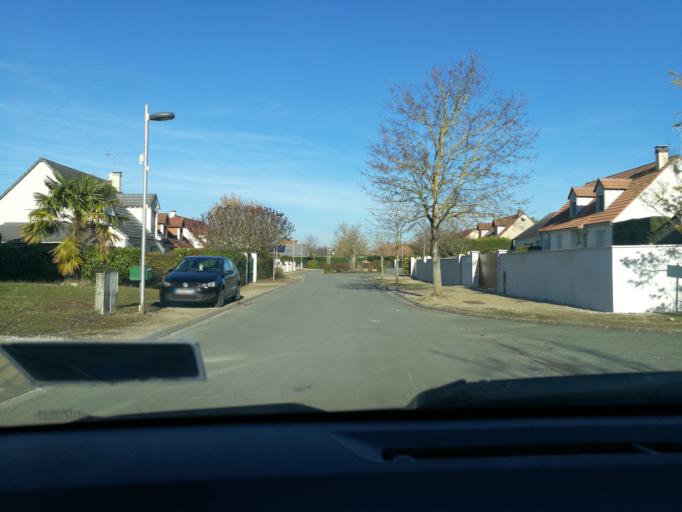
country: FR
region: Centre
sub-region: Departement du Loiret
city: Chaingy
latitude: 47.8821
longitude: 1.7781
